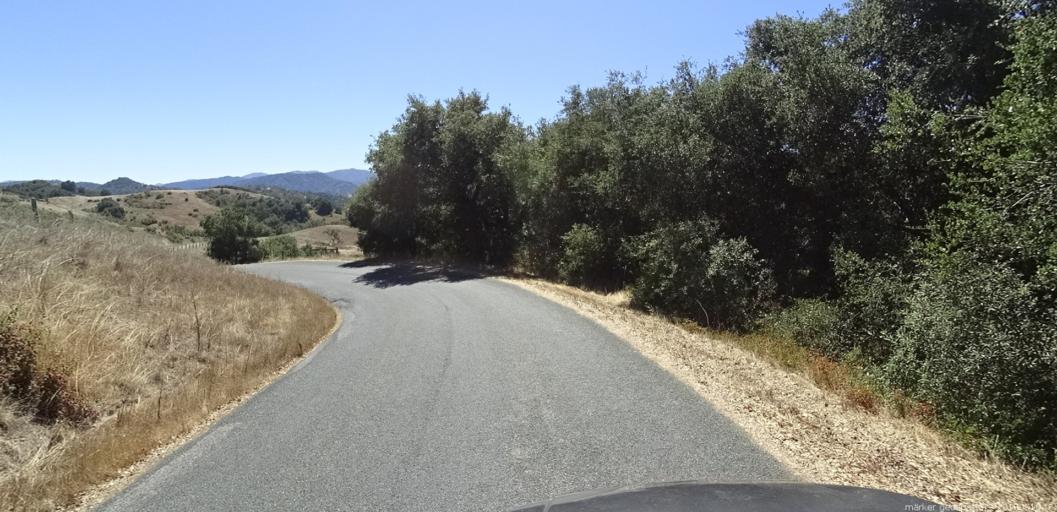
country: US
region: California
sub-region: Monterey County
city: Carmel Valley Village
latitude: 36.4685
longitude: -121.8012
